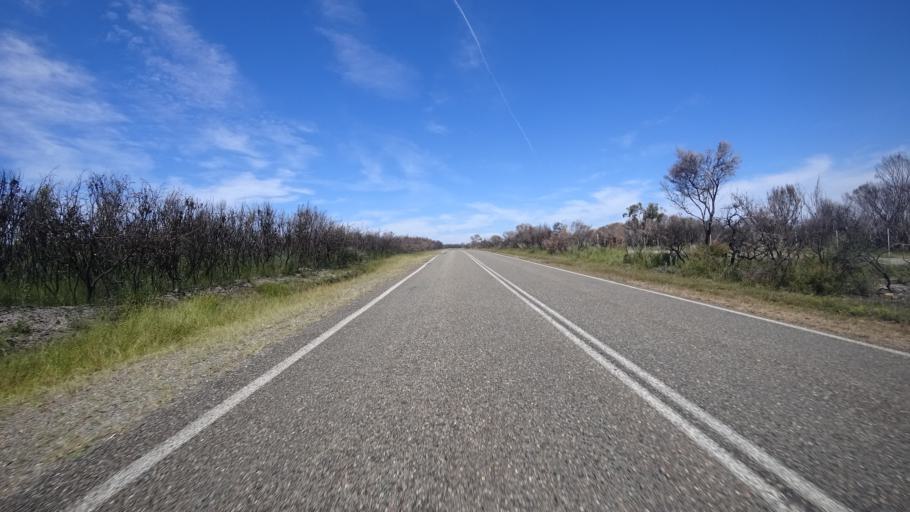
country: AU
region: New South Wales
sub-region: Shoalhaven Shire
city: Falls Creek
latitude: -35.1482
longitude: 150.7079
